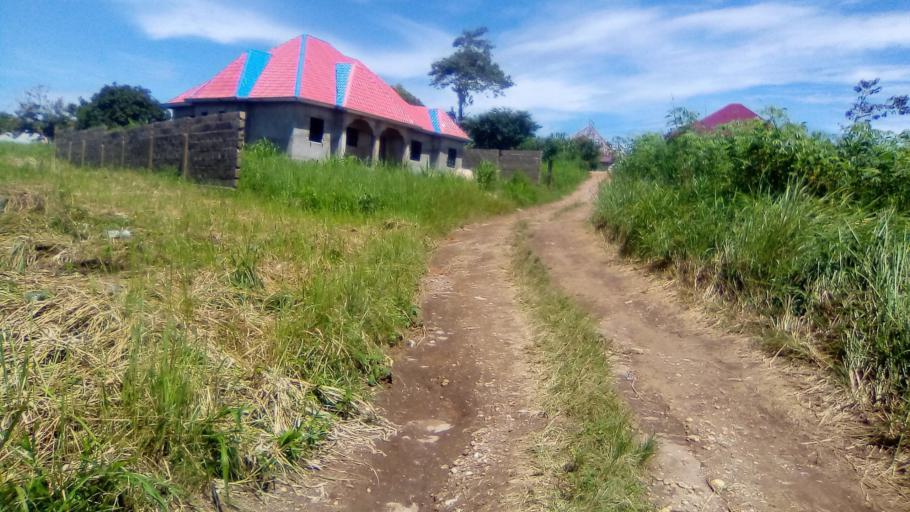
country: SL
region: Eastern Province
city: Simbakoro
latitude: 8.6305
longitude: -10.9946
